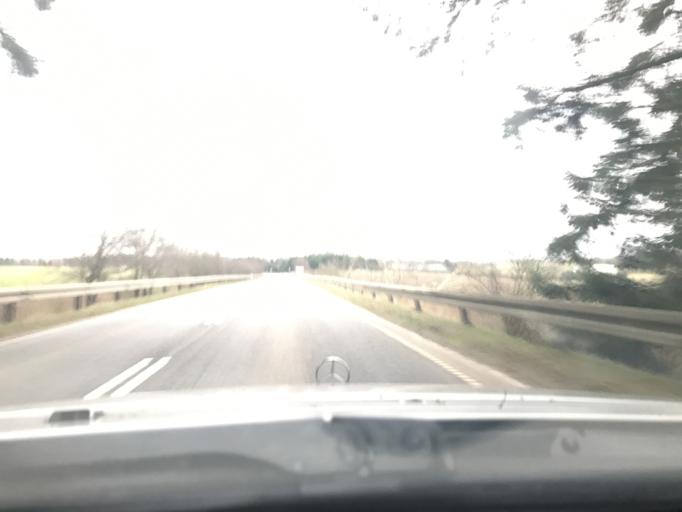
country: DK
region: South Denmark
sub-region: Tonder Kommune
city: Logumkloster
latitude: 55.1700
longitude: 8.9591
